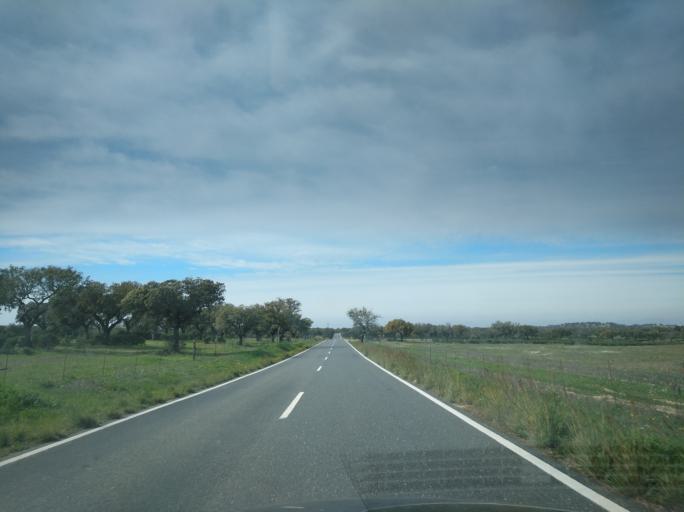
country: PT
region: Beja
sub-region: Mertola
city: Mertola
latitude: 37.7377
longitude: -7.7766
